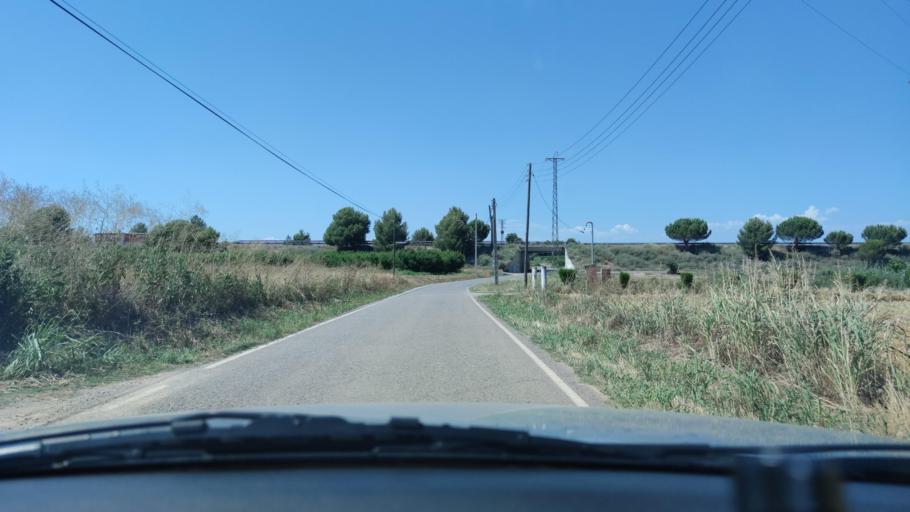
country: ES
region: Catalonia
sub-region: Provincia de Lleida
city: Torrefarrera
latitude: 41.6625
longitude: 0.6198
